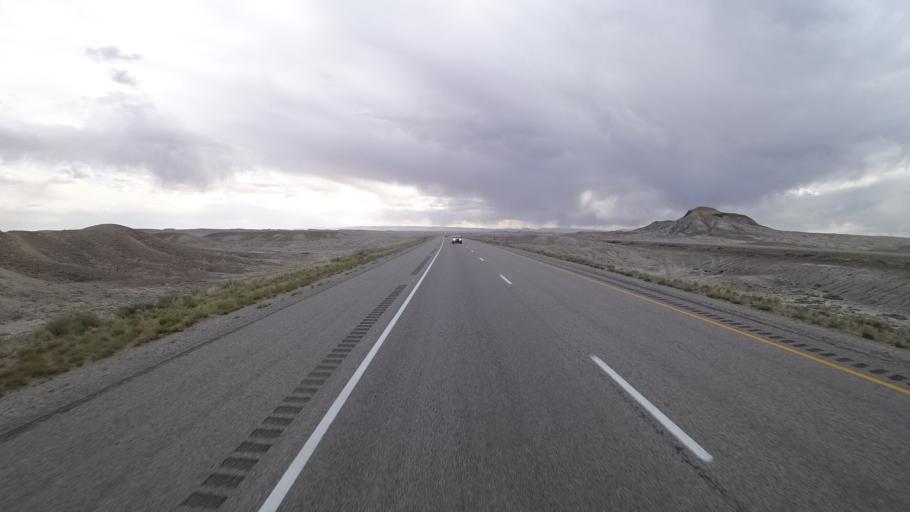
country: US
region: Utah
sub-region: Grand County
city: Moab
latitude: 38.9259
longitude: -109.9918
